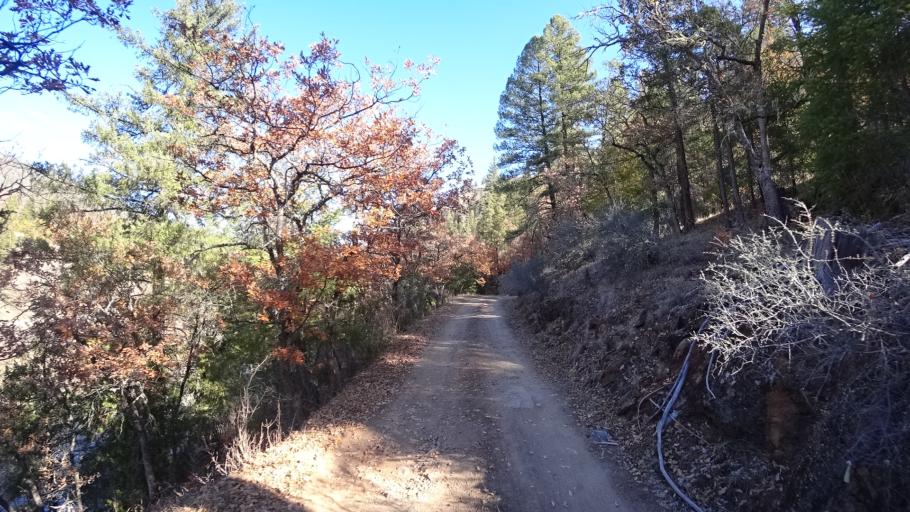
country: US
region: California
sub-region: Siskiyou County
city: Yreka
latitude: 41.8588
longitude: -122.7474
